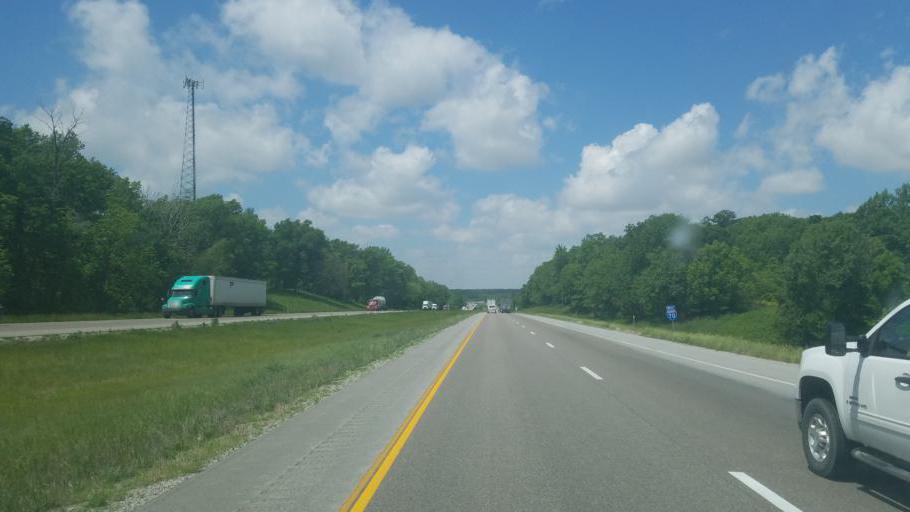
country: US
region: Illinois
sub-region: Cumberland County
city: Greenup
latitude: 39.2549
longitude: -88.1596
